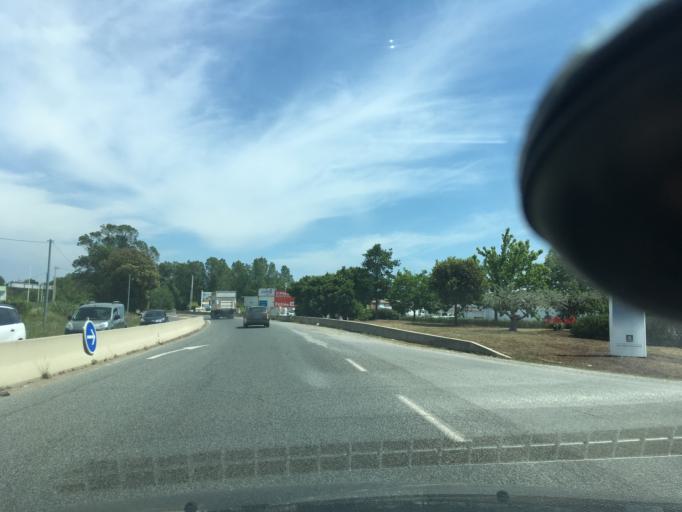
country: FR
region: Provence-Alpes-Cote d'Azur
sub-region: Departement du Var
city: Roquebrune-sur-Argens
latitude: 43.4625
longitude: 6.6441
